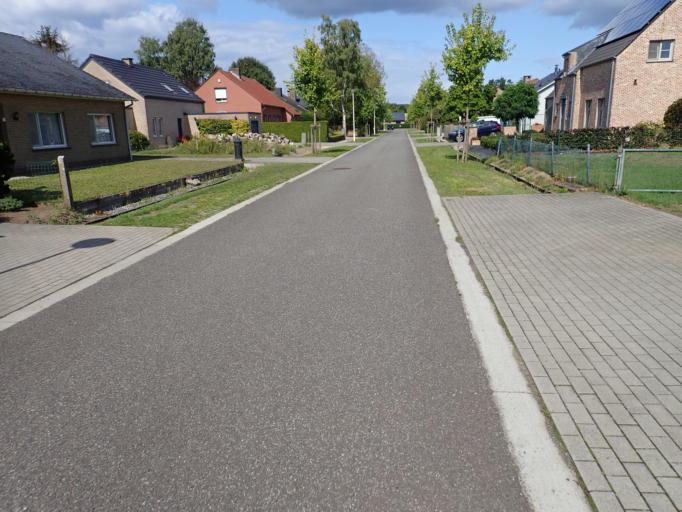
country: BE
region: Flanders
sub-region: Provincie Antwerpen
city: Zandhoven
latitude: 51.2443
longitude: 4.6486
